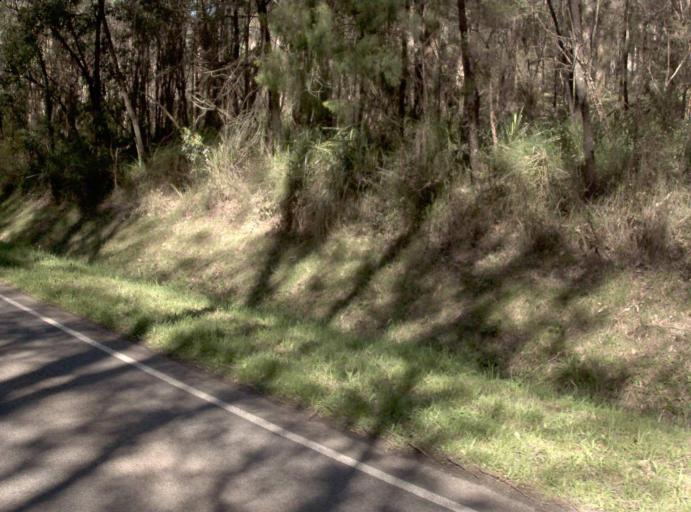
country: AU
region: Victoria
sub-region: Yarra Ranges
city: Millgrove
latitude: -37.8822
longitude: 145.8604
